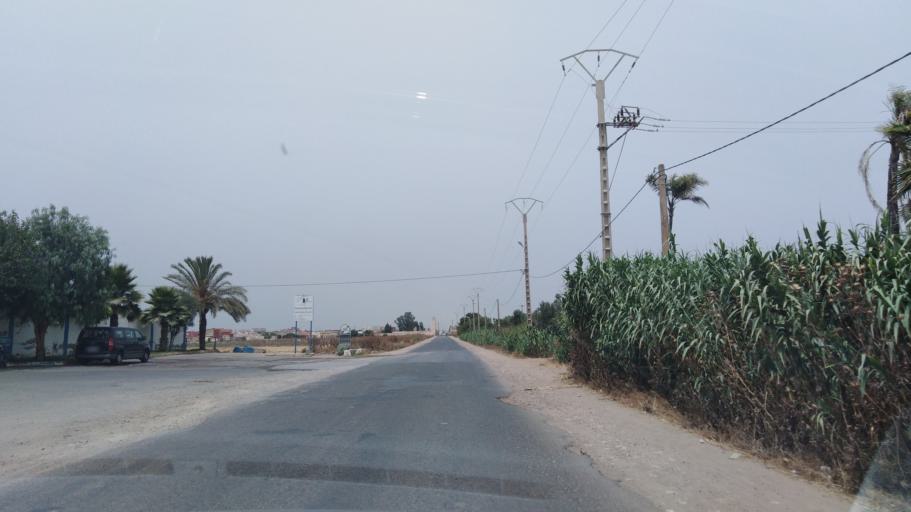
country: MA
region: Grand Casablanca
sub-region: Mediouna
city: Mediouna
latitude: 33.4105
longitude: -7.5148
